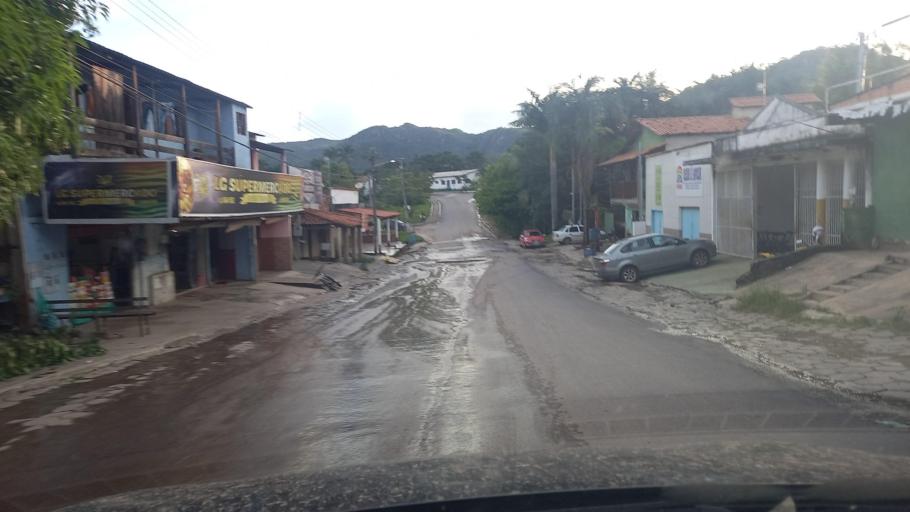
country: BR
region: Goias
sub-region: Cavalcante
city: Cavalcante
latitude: -13.7946
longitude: -47.4601
